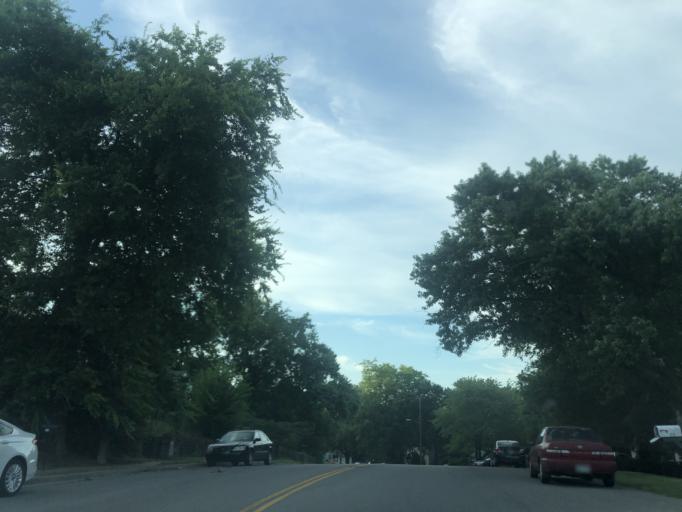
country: US
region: Tennessee
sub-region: Davidson County
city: Nashville
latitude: 36.1635
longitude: -86.7469
